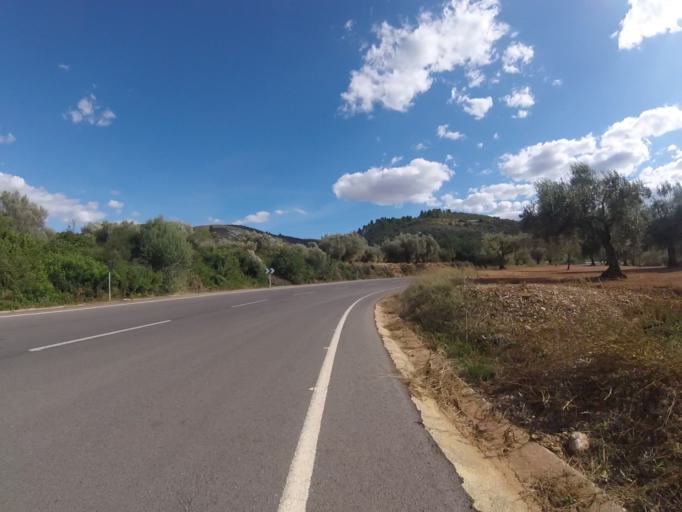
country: ES
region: Valencia
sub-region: Provincia de Castello
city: Cuevas de Vinroma
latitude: 40.3002
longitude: 0.1672
